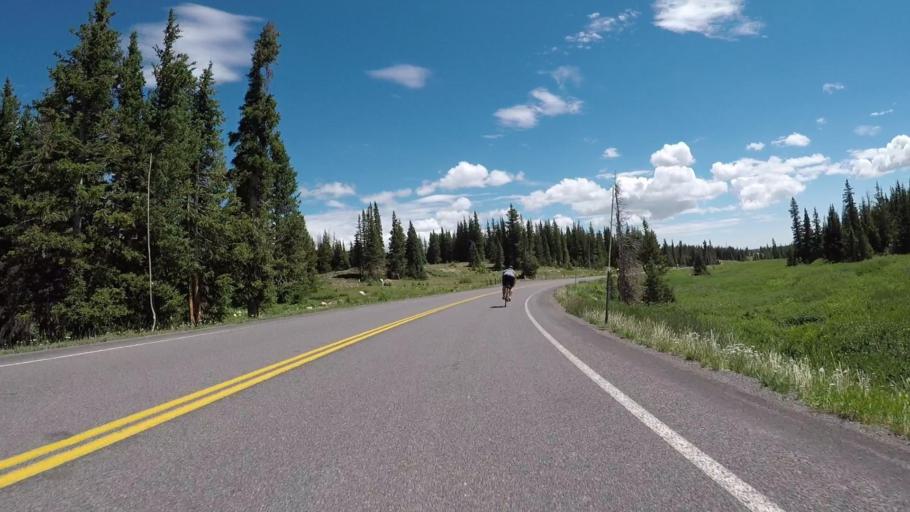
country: US
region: Wyoming
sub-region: Carbon County
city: Saratoga
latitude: 41.3506
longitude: -106.2876
